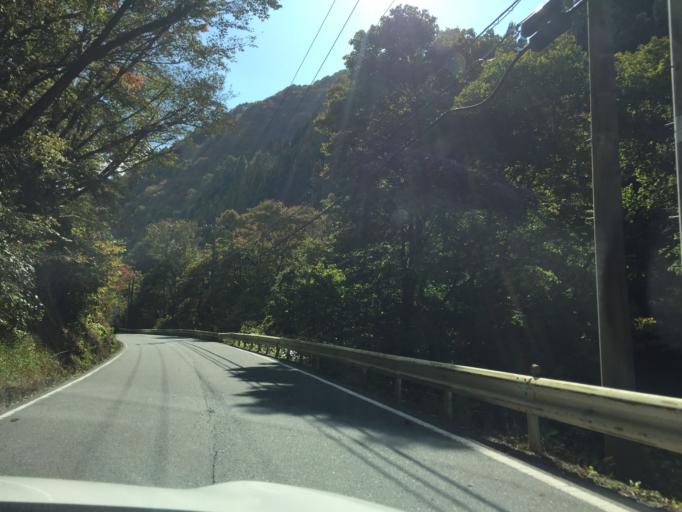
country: JP
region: Fukushima
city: Namie
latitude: 37.3486
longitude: 140.8846
